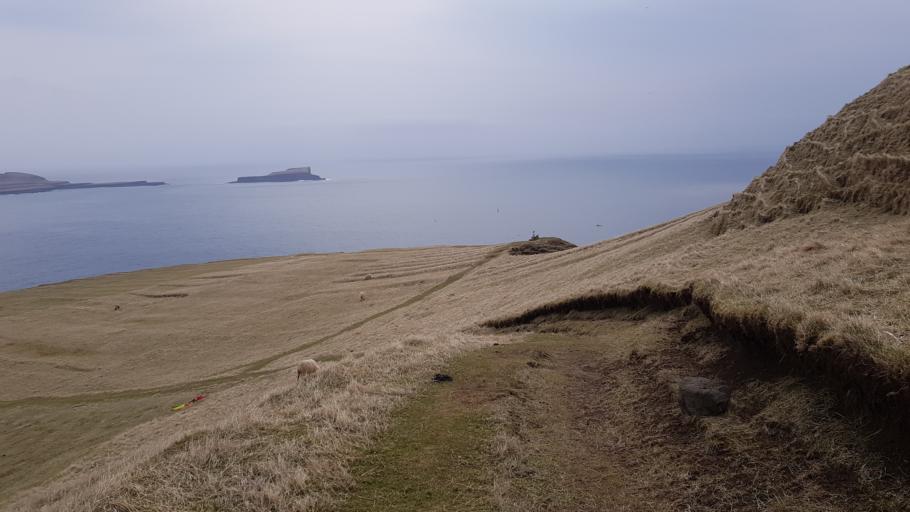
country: FO
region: Vagar
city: Sorvagur
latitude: 62.1113
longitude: -7.4425
